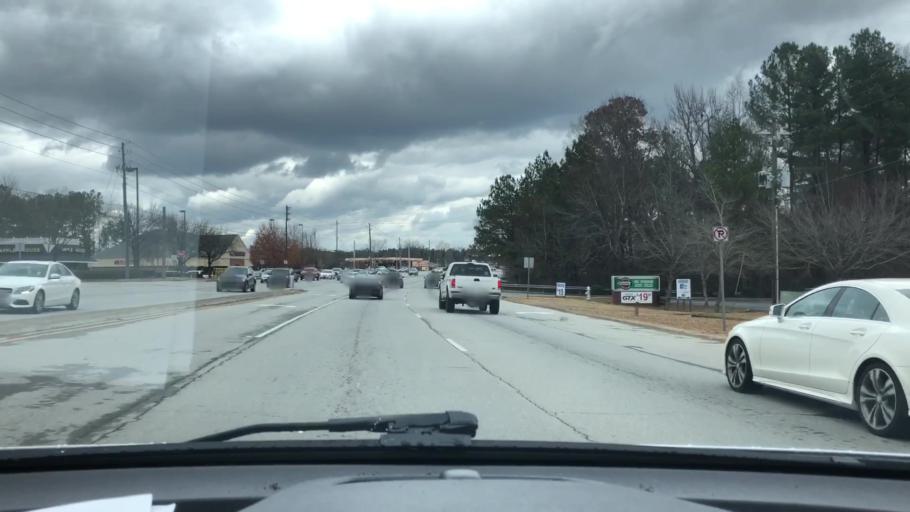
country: US
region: Georgia
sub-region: Gwinnett County
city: Duluth
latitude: 34.0022
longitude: -84.1693
